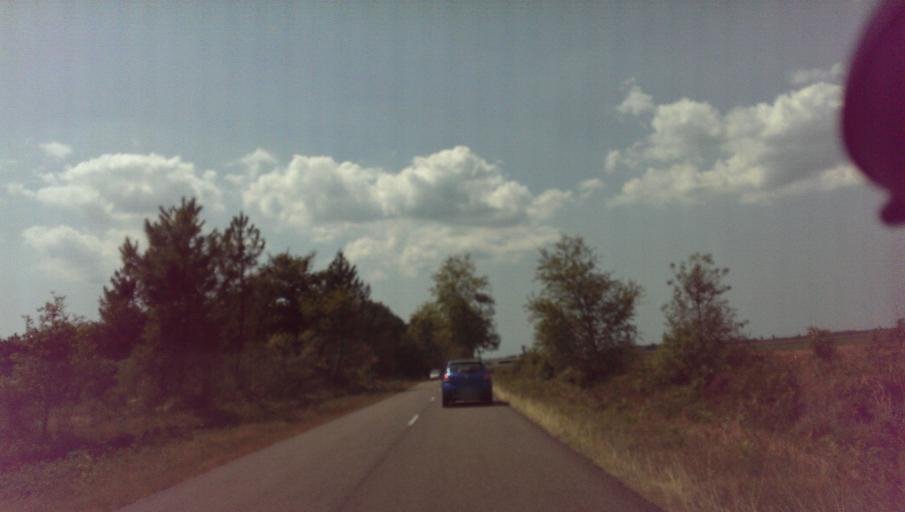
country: FR
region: Aquitaine
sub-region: Departement des Landes
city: Sabres
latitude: 44.1174
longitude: -0.6329
